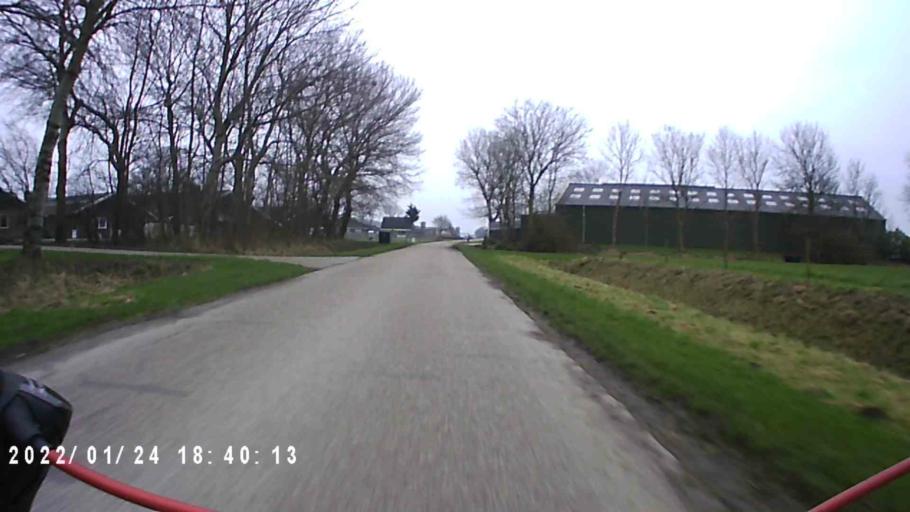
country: NL
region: Groningen
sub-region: Gemeente De Marne
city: Ulrum
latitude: 53.3465
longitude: 6.3442
